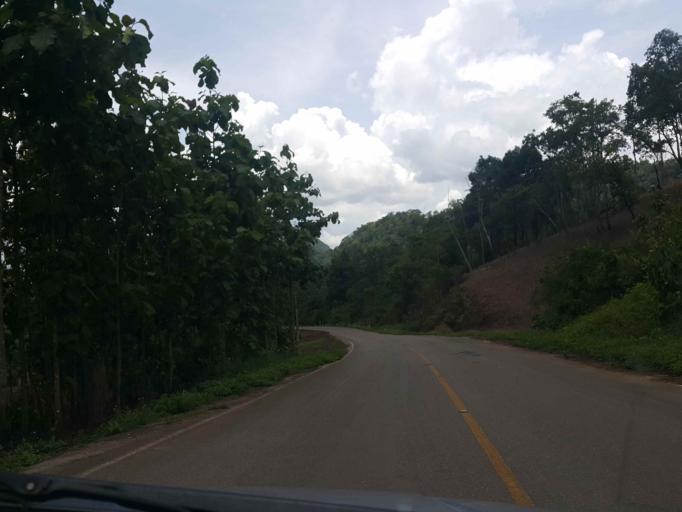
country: TH
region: Phayao
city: Chiang Muan
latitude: 18.9043
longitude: 100.1223
